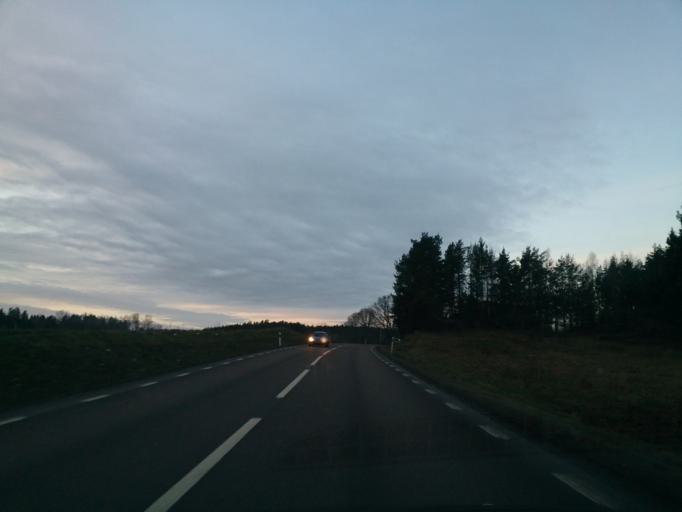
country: SE
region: OEstergoetland
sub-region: Linkopings Kommun
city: Sturefors
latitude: 58.3083
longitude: 15.8818
